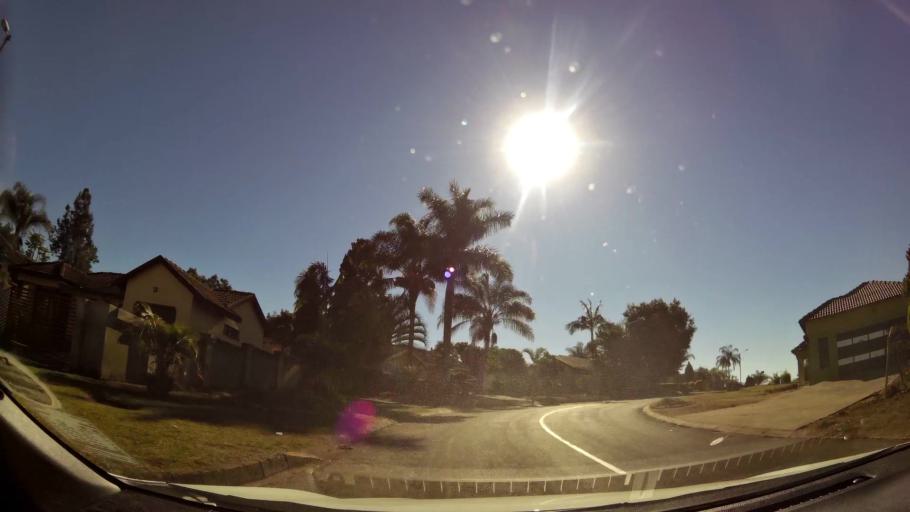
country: ZA
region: Limpopo
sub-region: Mopani District Municipality
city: Tzaneen
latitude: -23.8460
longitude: 30.1631
